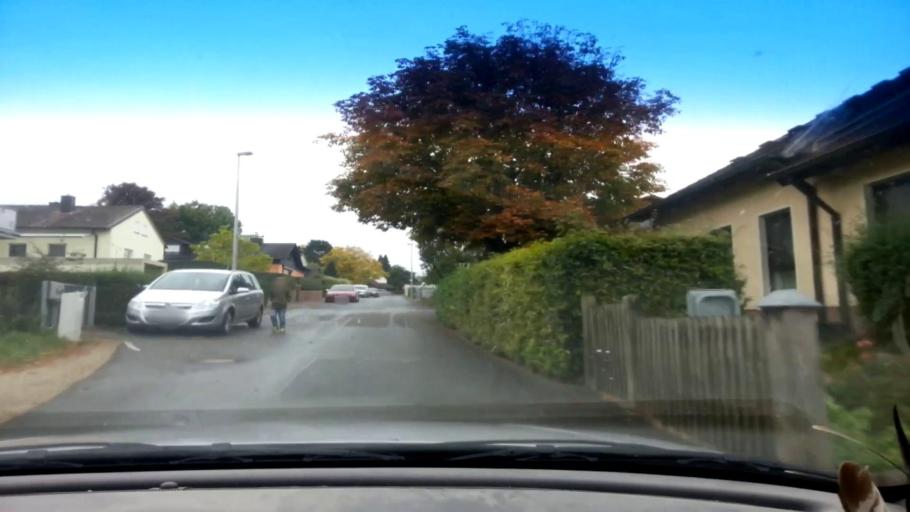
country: DE
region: Bavaria
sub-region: Upper Franconia
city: Litzendorf
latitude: 49.9096
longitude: 11.0055
